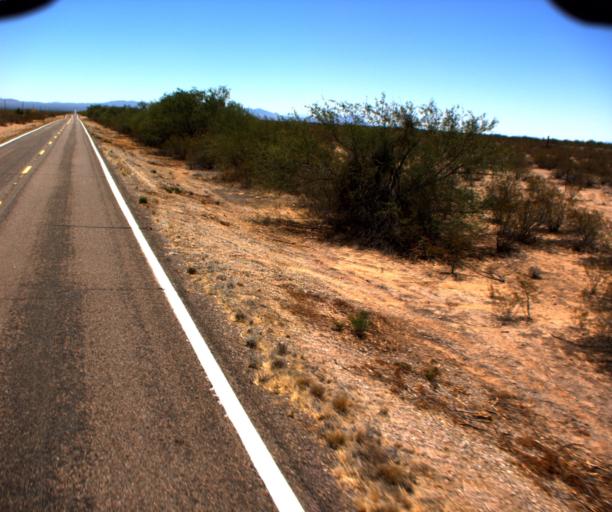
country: US
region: Arizona
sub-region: Pima County
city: Ajo
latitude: 32.2016
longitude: -112.5067
